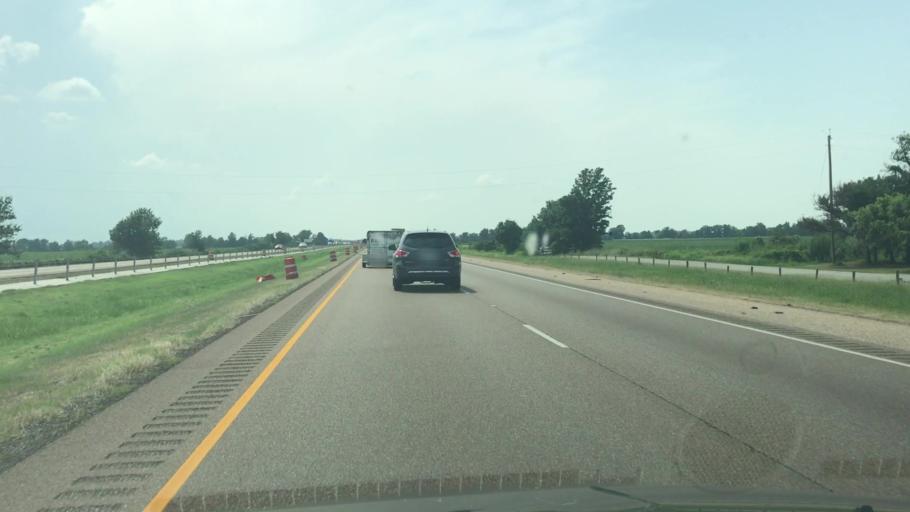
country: US
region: Arkansas
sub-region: Crittenden County
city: Earle
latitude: 35.1507
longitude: -90.3806
